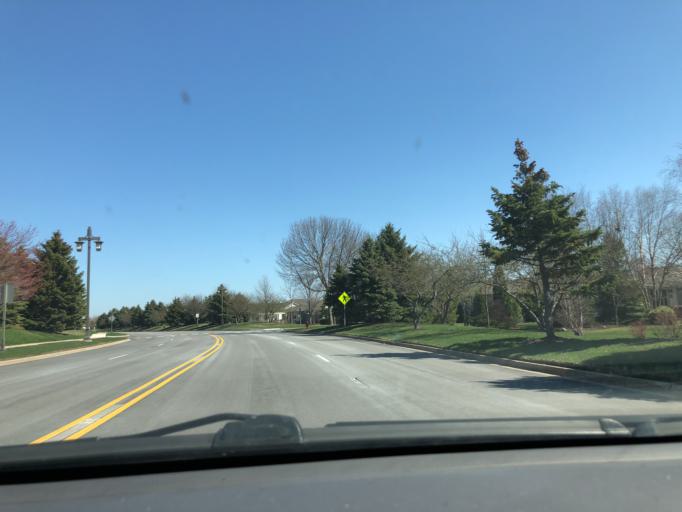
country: US
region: Illinois
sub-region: McHenry County
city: Huntley
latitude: 42.1561
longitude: -88.4509
